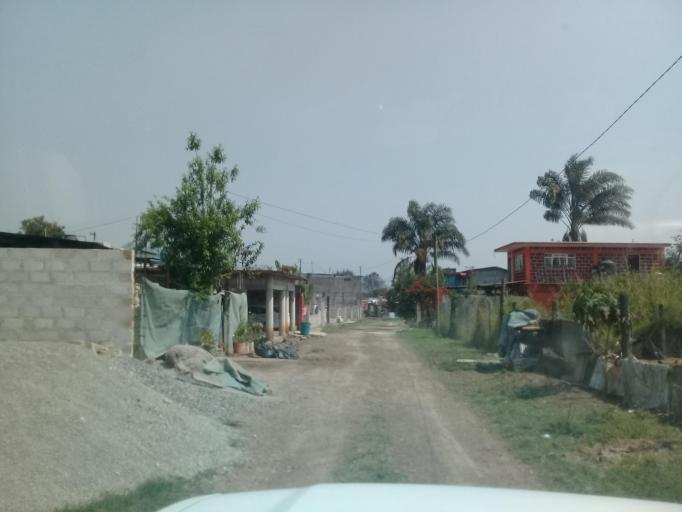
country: MX
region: Veracruz
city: Ixtac Zoquitlan
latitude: 18.8723
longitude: -97.0604
